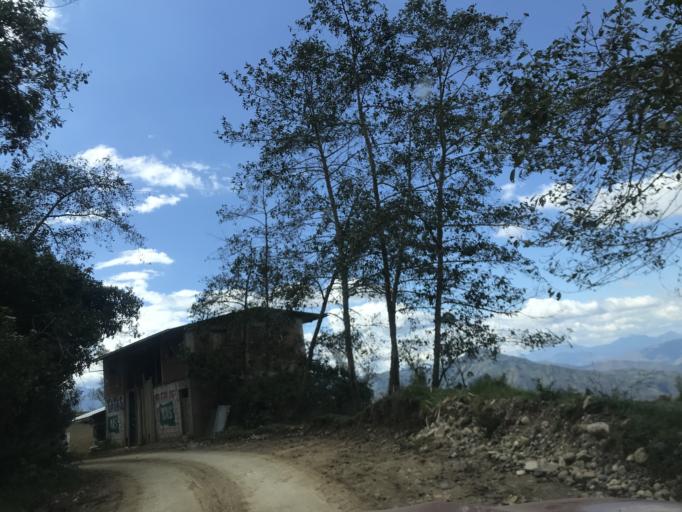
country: PE
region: Cajamarca
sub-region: Provincia de Chota
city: Querocoto
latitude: -6.3362
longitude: -79.0670
